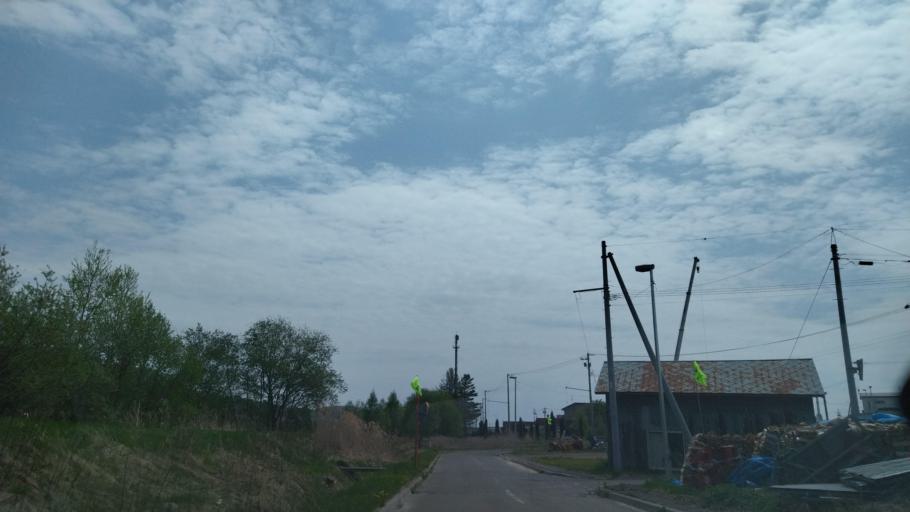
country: JP
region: Hokkaido
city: Otofuke
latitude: 43.2524
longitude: 143.5496
